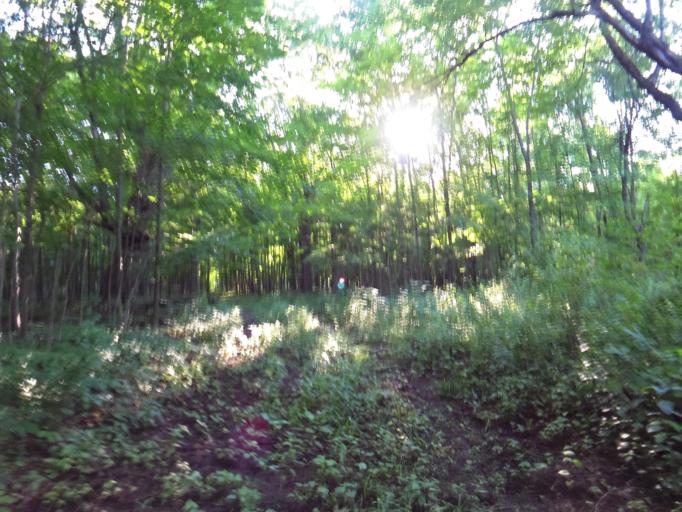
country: CA
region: Ontario
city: Bells Corners
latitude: 45.2975
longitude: -75.8029
